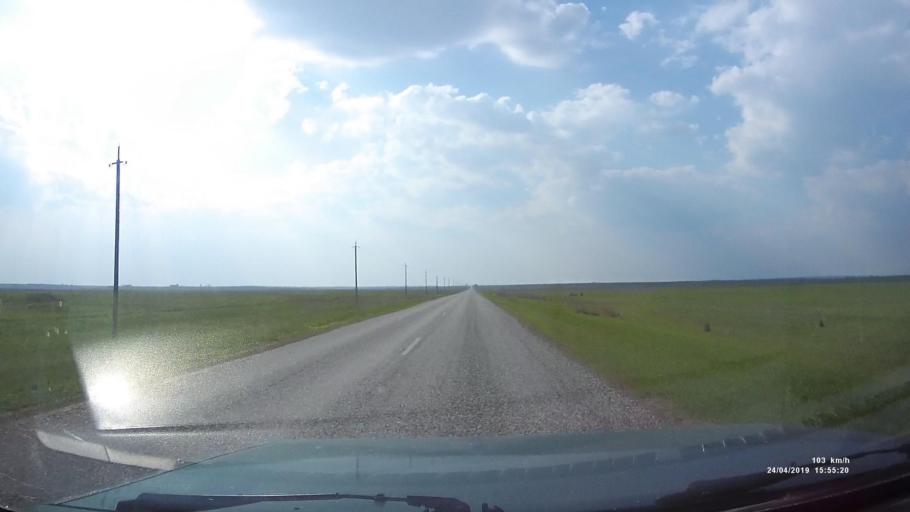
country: RU
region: Kalmykiya
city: Yashalta
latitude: 46.5896
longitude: 42.5516
